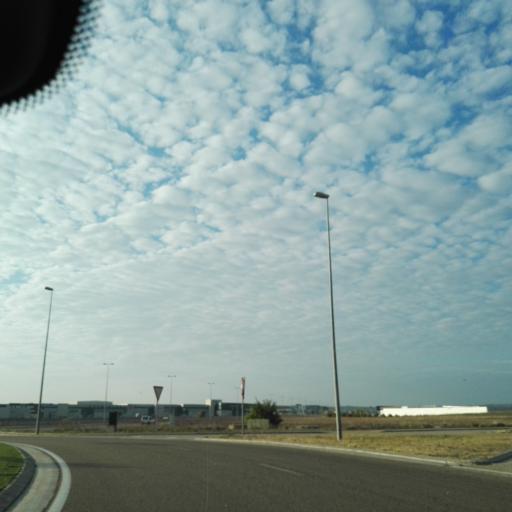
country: ES
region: Aragon
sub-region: Provincia de Zaragoza
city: Utebo
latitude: 41.6534
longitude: -1.0006
